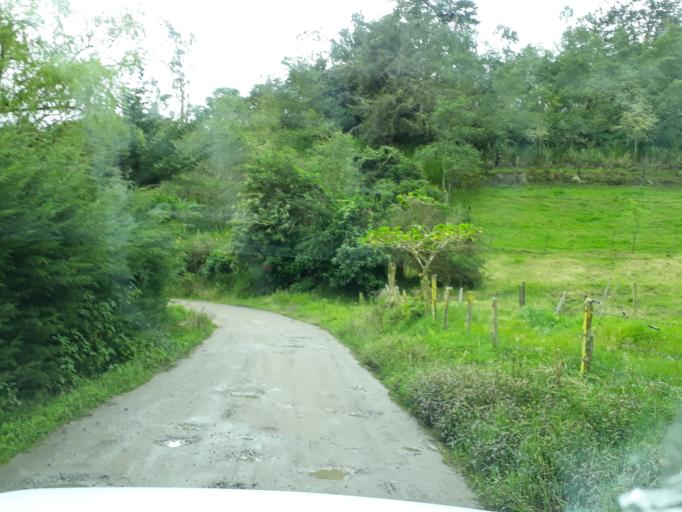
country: CO
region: Cundinamarca
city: Junin
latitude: 4.7966
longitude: -73.6603
